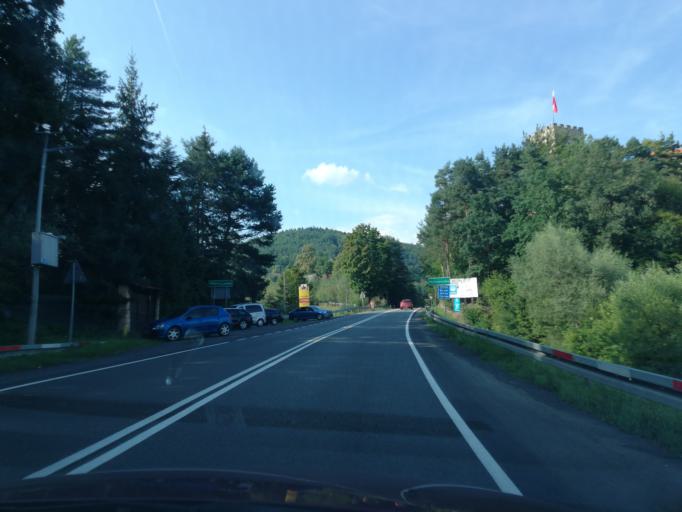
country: PL
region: Lesser Poland Voivodeship
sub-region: Powiat nowosadecki
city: Lososina Dolna
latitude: 49.7953
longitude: 20.6445
